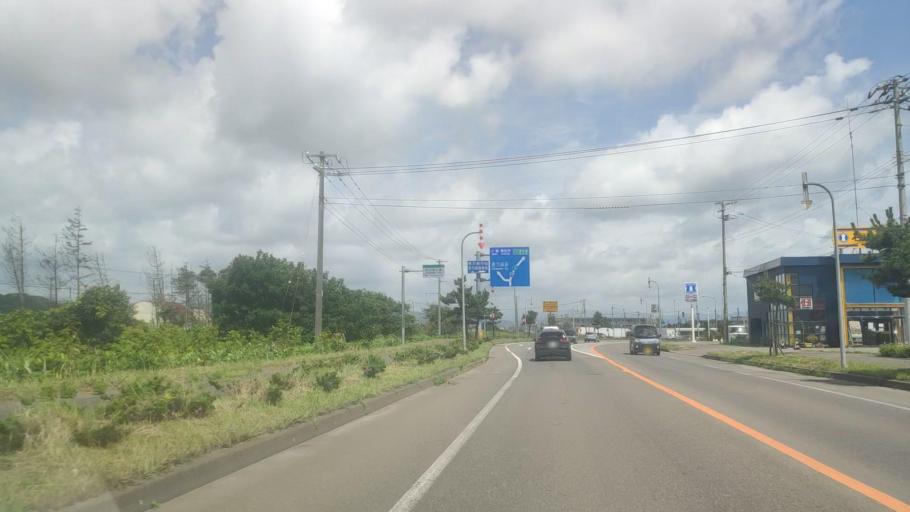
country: JP
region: Hokkaido
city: Niseko Town
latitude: 42.4994
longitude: 140.3653
